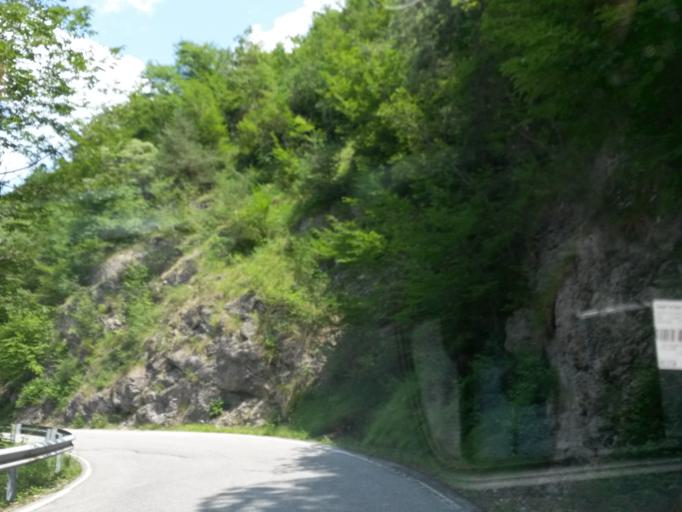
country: IT
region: Lombardy
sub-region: Provincia di Brescia
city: Valvestino
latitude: 45.7323
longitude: 10.6072
